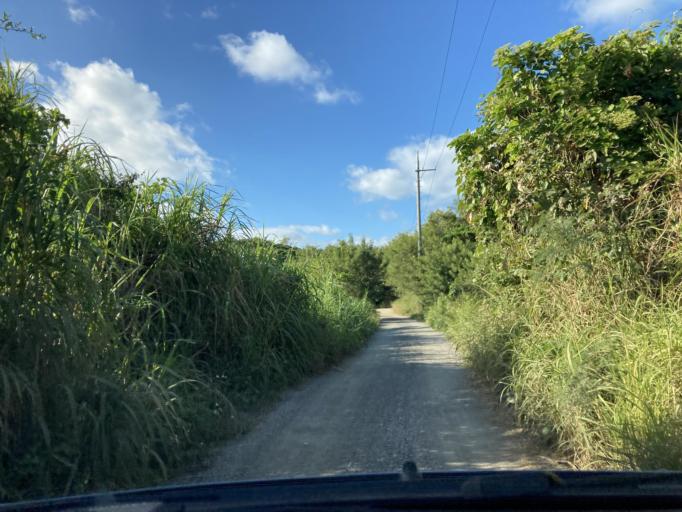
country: JP
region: Okinawa
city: Katsuren-haebaru
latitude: 26.3195
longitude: 127.9245
